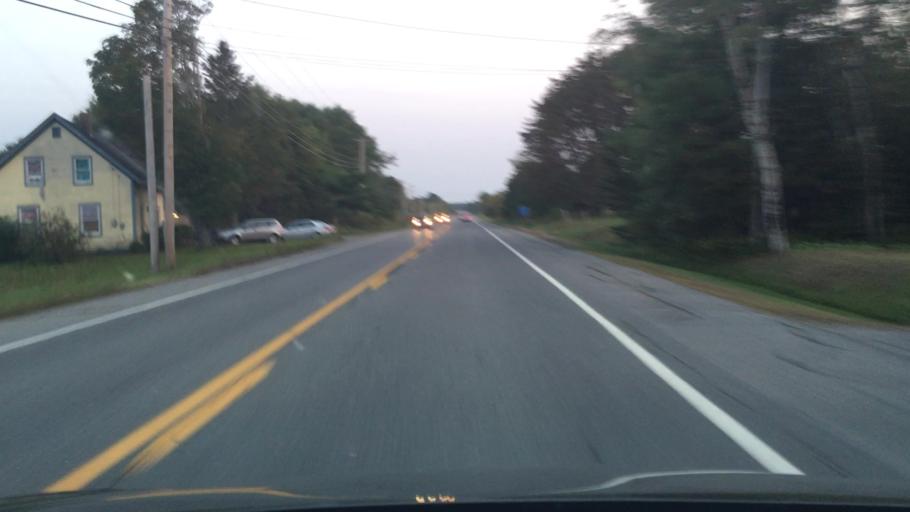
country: US
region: Maine
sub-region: Waldo County
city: Stockton Springs
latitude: 44.5367
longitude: -68.8611
